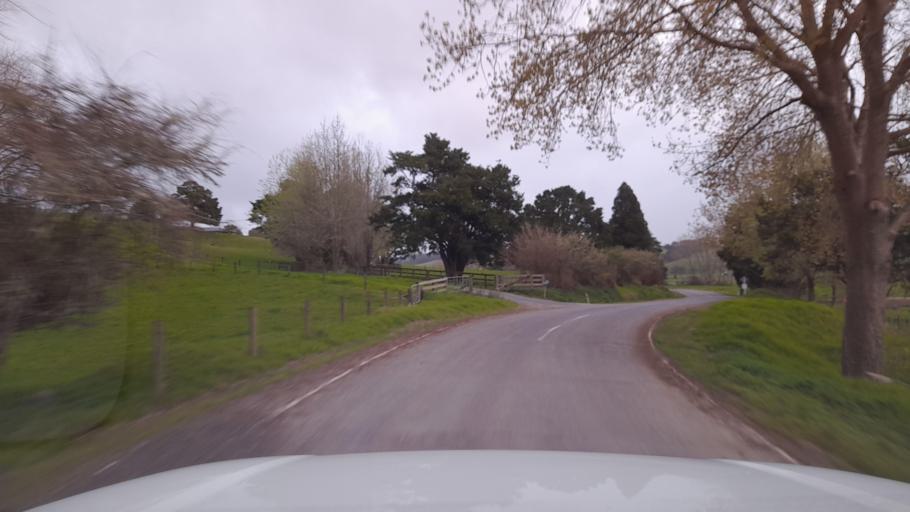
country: NZ
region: Northland
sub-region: Whangarei
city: Maungatapere
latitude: -35.6322
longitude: 174.1993
